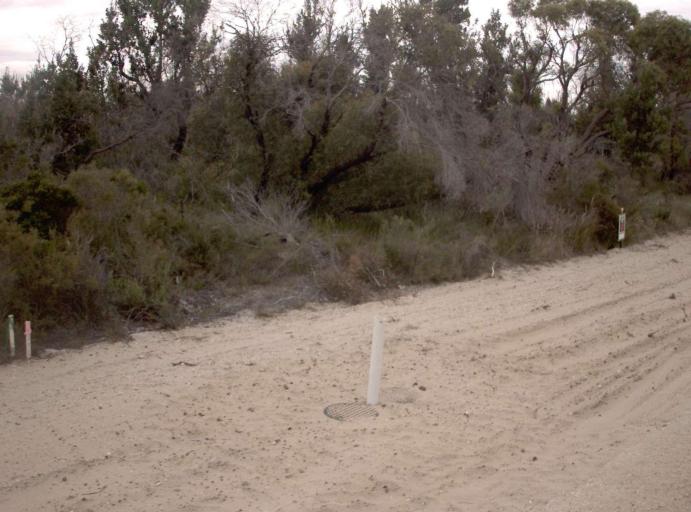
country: AU
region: Victoria
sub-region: East Gippsland
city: Bairnsdale
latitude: -38.1110
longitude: 147.4691
